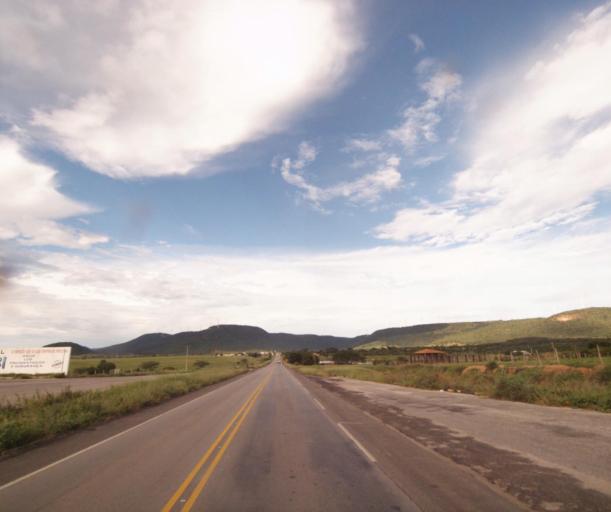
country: BR
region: Bahia
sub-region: Guanambi
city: Guanambi
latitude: -14.1770
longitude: -42.7311
